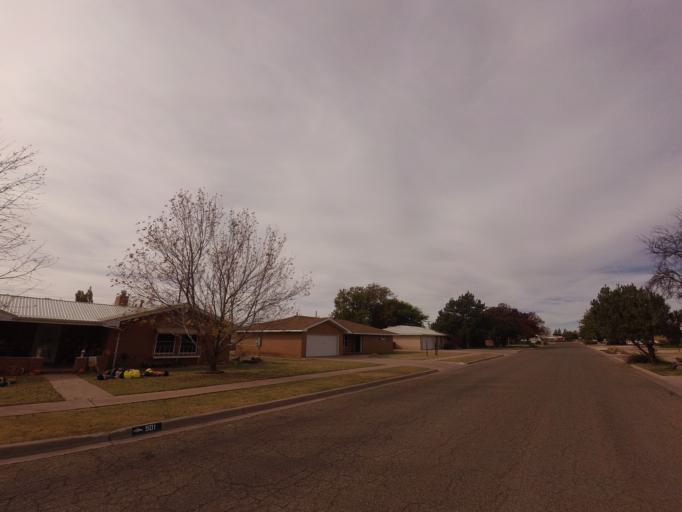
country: US
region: New Mexico
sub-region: Curry County
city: Clovis
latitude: 34.4213
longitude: -103.2119
